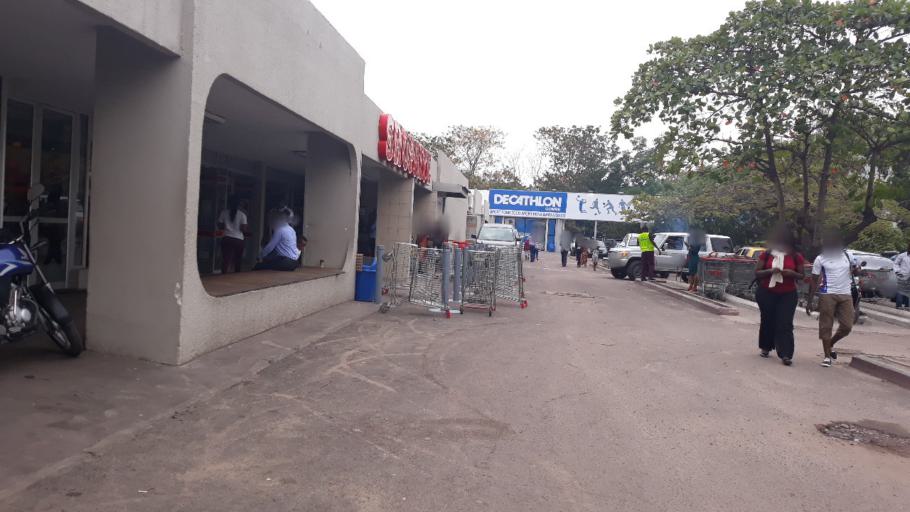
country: CD
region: Kinshasa
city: Kinshasa
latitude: -4.3289
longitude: 15.2750
